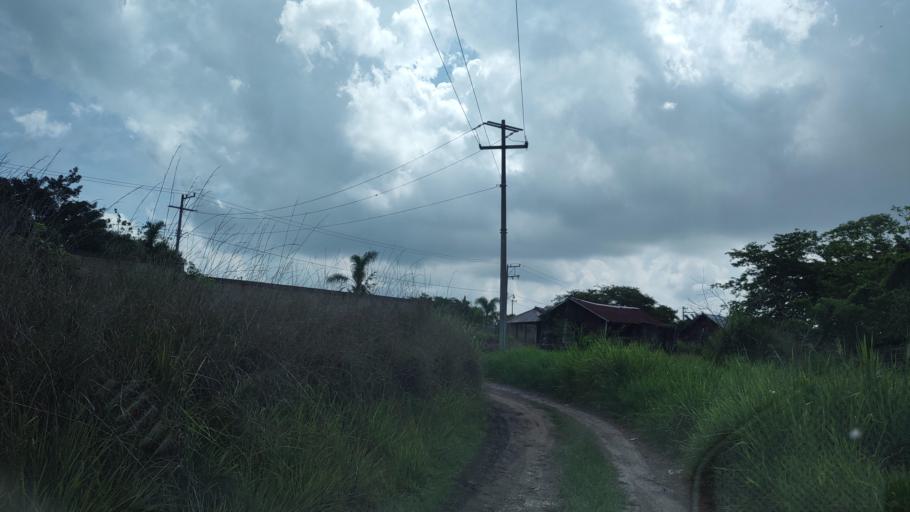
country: MX
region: Veracruz
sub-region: Emiliano Zapata
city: Dos Rios
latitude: 19.4589
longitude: -96.8068
